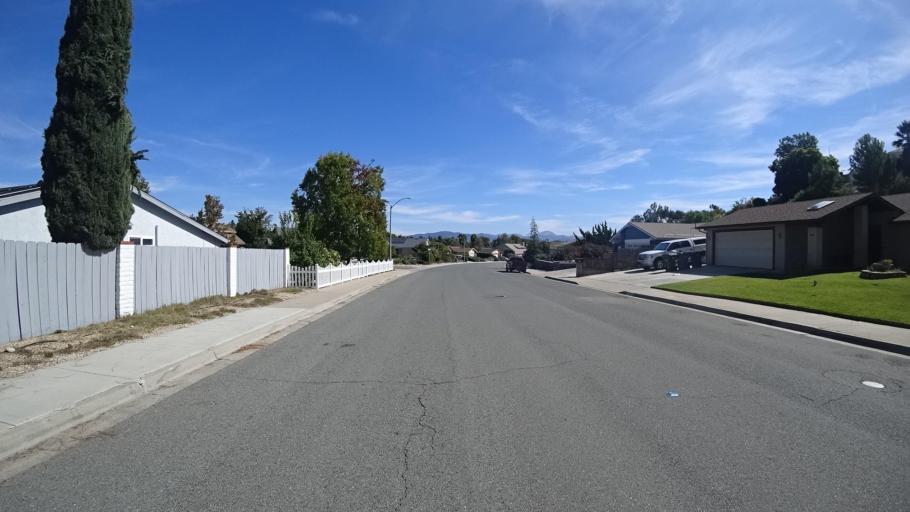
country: US
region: California
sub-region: San Diego County
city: Casa de Oro-Mount Helix
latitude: 32.7531
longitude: -116.9711
